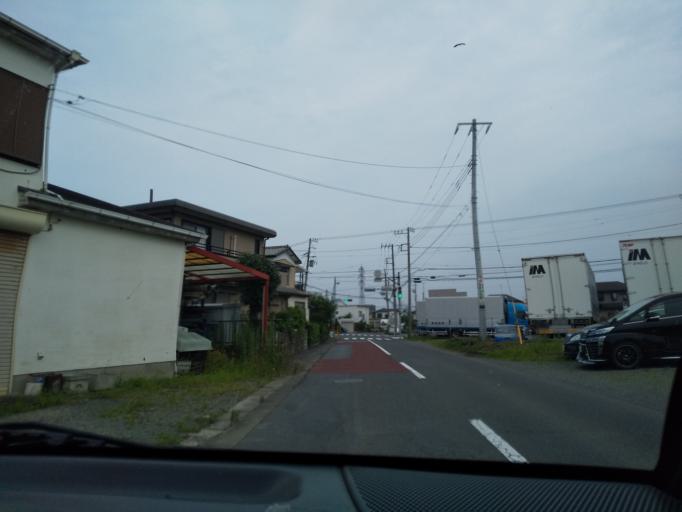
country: JP
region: Kanagawa
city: Atsugi
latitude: 35.3931
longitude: 139.3855
